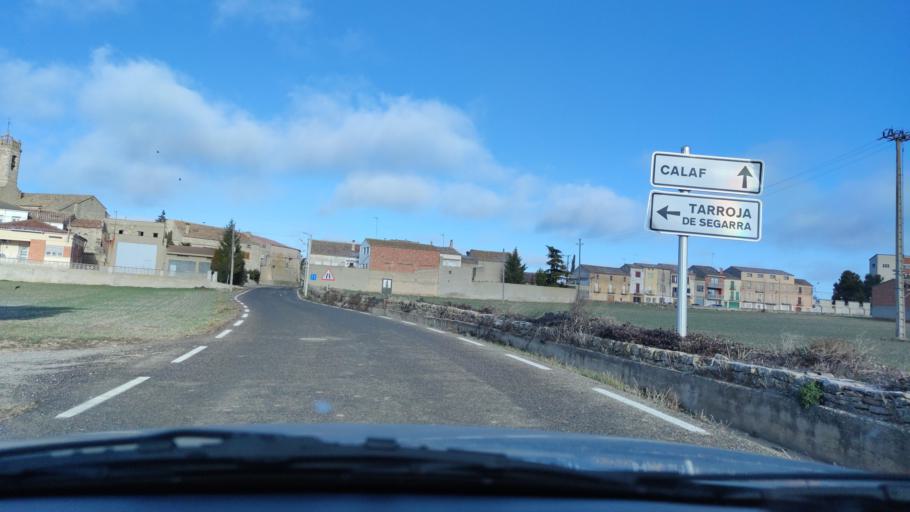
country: ES
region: Catalonia
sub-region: Provincia de Lleida
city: Ivorra
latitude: 41.7236
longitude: 1.3597
